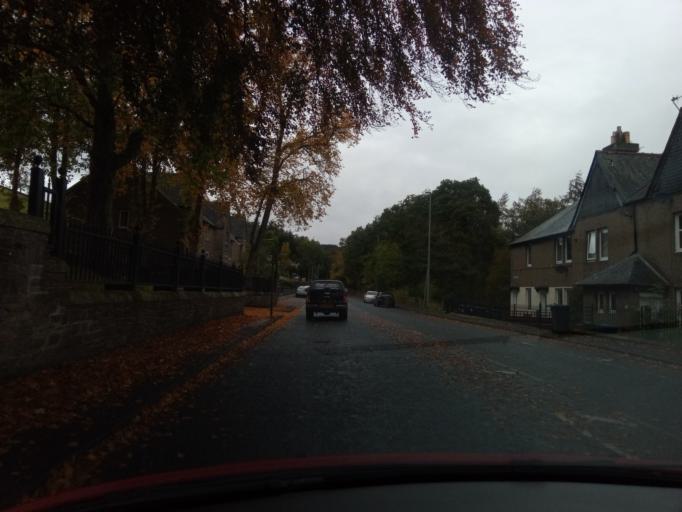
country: GB
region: Scotland
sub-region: The Scottish Borders
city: Galashiels
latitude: 55.6265
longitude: -2.8344
